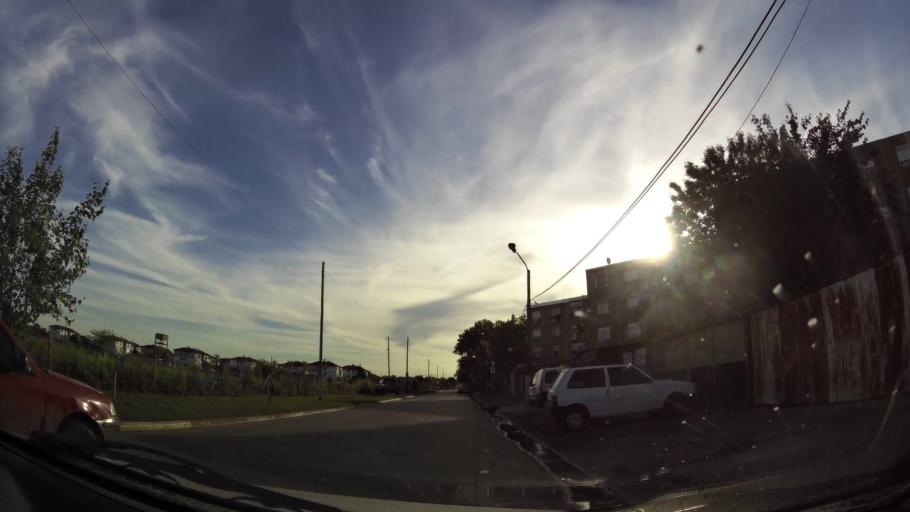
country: AR
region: Buenos Aires
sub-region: Partido de Almirante Brown
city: Adrogue
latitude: -34.8191
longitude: -58.3372
